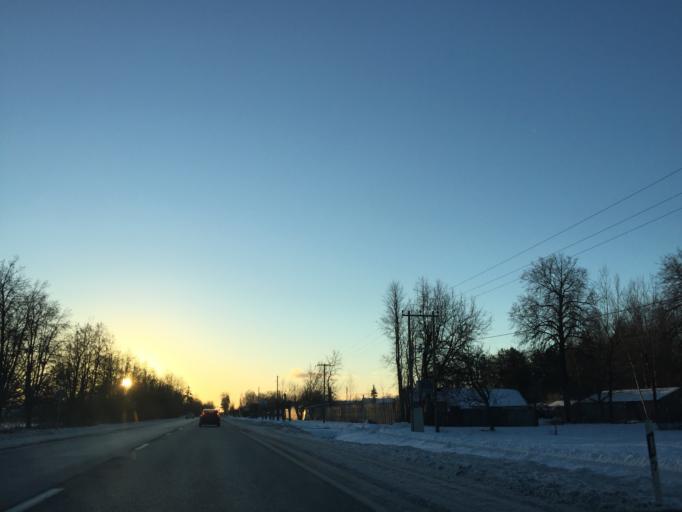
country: LV
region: Ogre
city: Ogre
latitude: 56.7837
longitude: 24.6473
